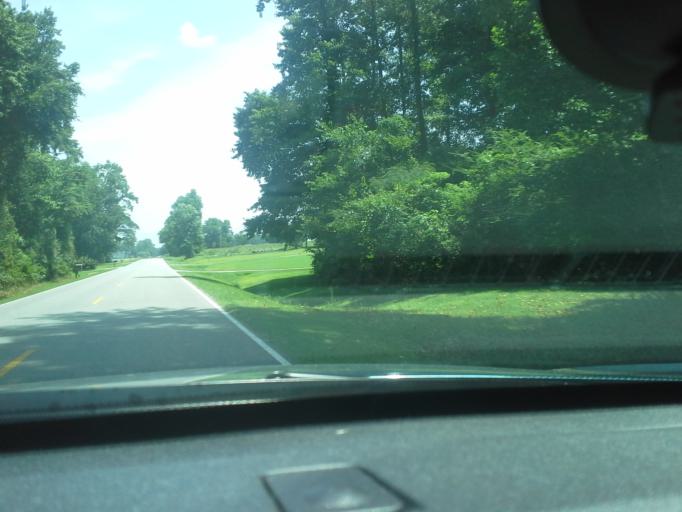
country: US
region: North Carolina
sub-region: Washington County
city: Plymouth
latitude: 35.9060
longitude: -76.6688
